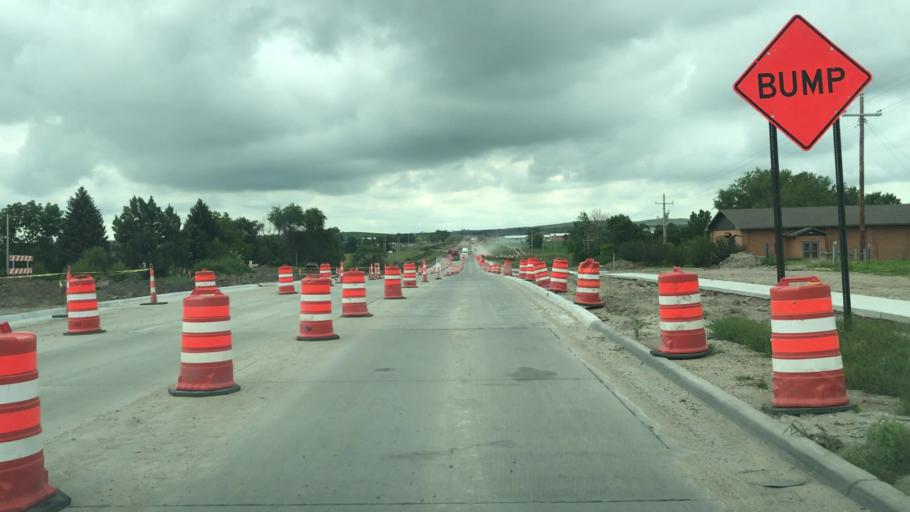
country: US
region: South Dakota
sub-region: Todd County
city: Mission
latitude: 43.3054
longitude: -100.6527
